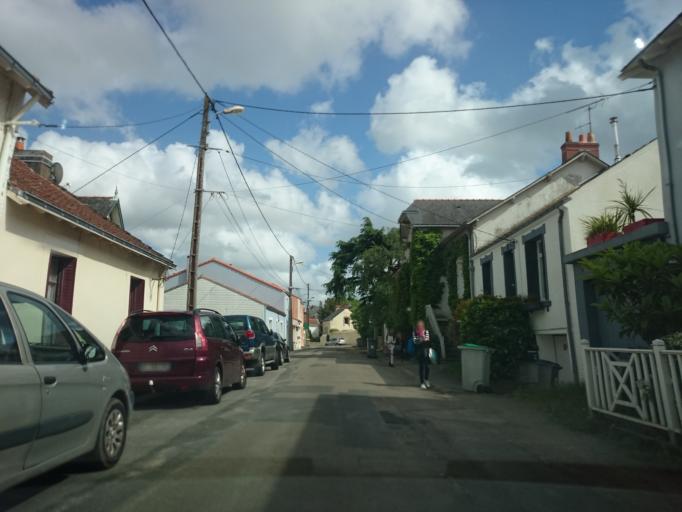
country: FR
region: Pays de la Loire
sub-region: Departement de la Loire-Atlantique
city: La Montagne
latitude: 47.1929
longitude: -1.6892
